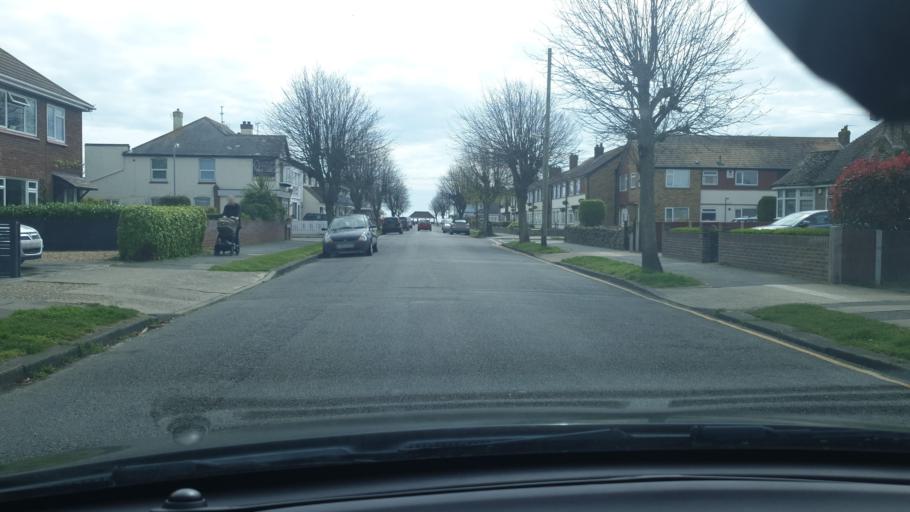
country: GB
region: England
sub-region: Essex
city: Clacton-on-Sea
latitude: 51.8003
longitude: 1.1835
